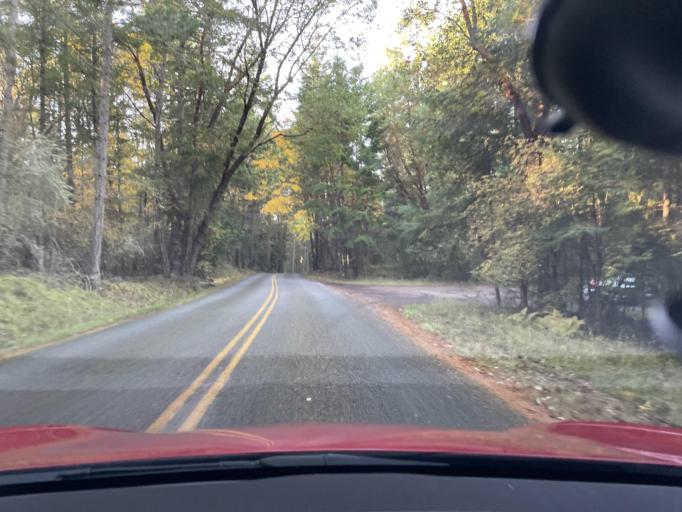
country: US
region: Washington
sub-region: San Juan County
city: Friday Harbor
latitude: 48.5202
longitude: -123.1439
